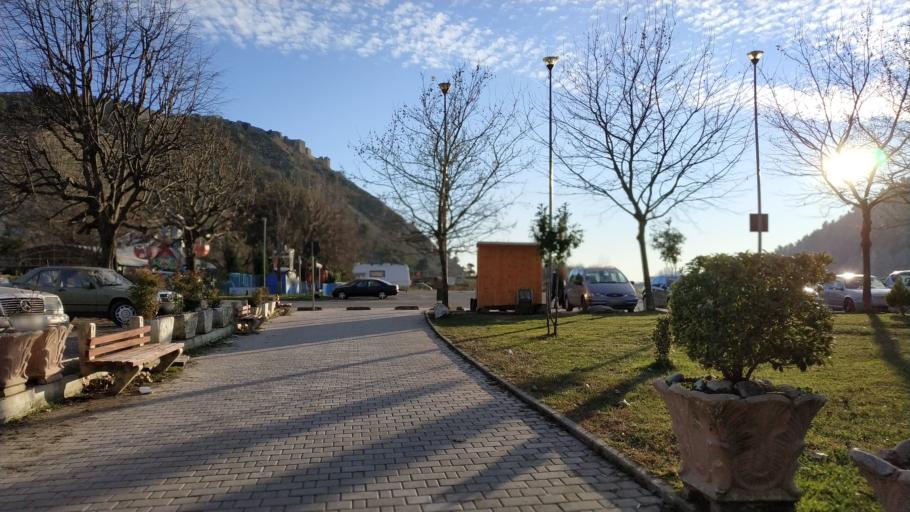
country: AL
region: Shkoder
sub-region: Rrethi i Shkodres
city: Shkoder
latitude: 42.0508
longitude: 19.4926
